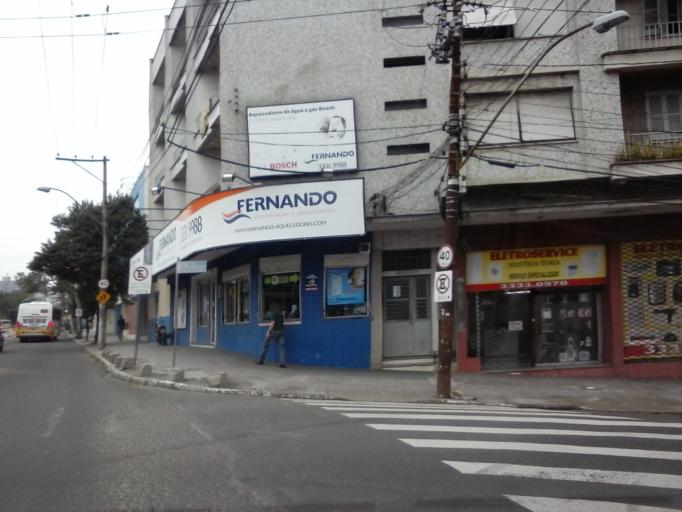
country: BR
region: Rio Grande do Sul
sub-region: Porto Alegre
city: Porto Alegre
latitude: -30.0439
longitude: -51.1856
